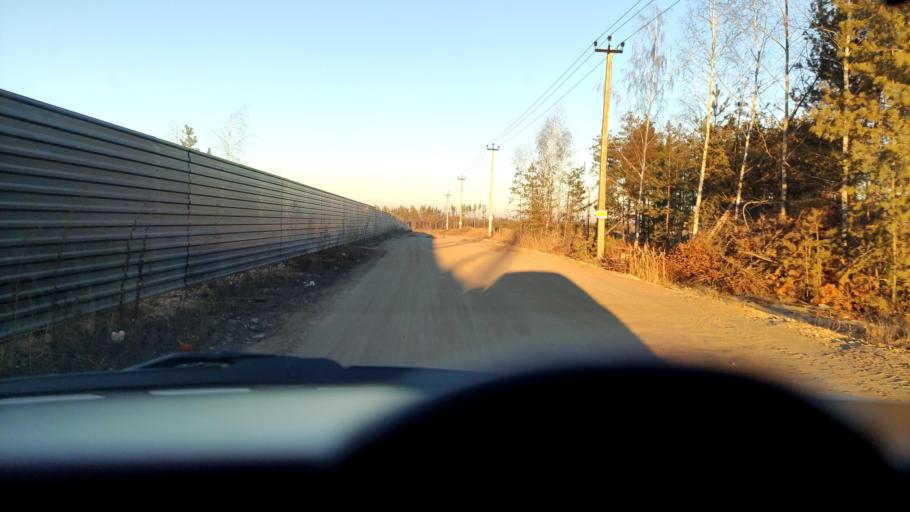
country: RU
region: Voronezj
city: Podgornoye
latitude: 51.7498
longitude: 39.1419
